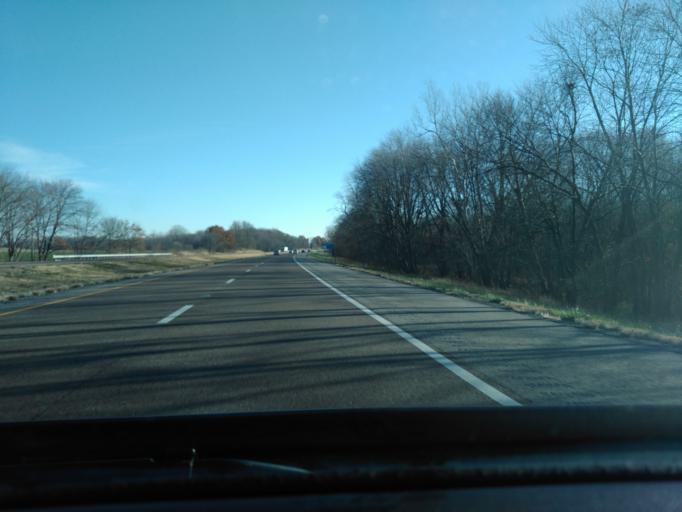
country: US
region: Illinois
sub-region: Madison County
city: Troy
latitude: 38.7608
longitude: -89.8306
